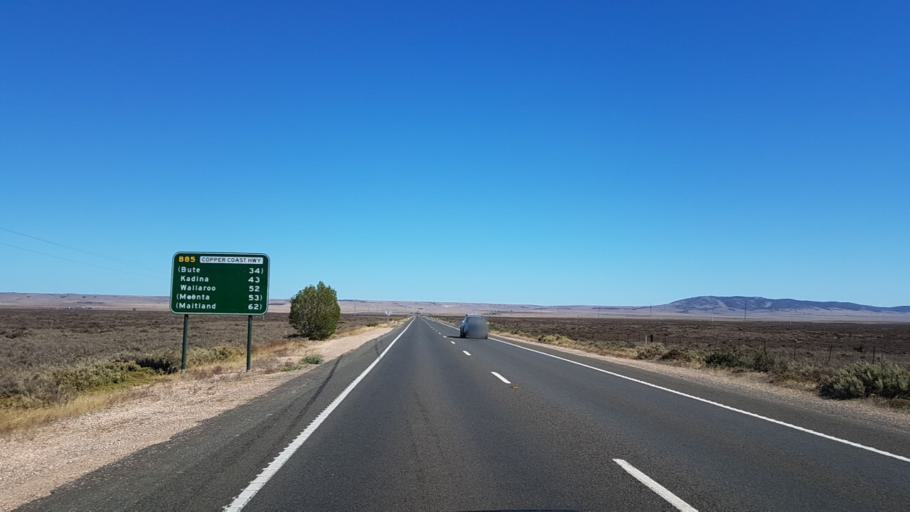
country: AU
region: South Australia
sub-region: Wakefield
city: Balaklava
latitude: -34.1138
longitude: 138.1239
